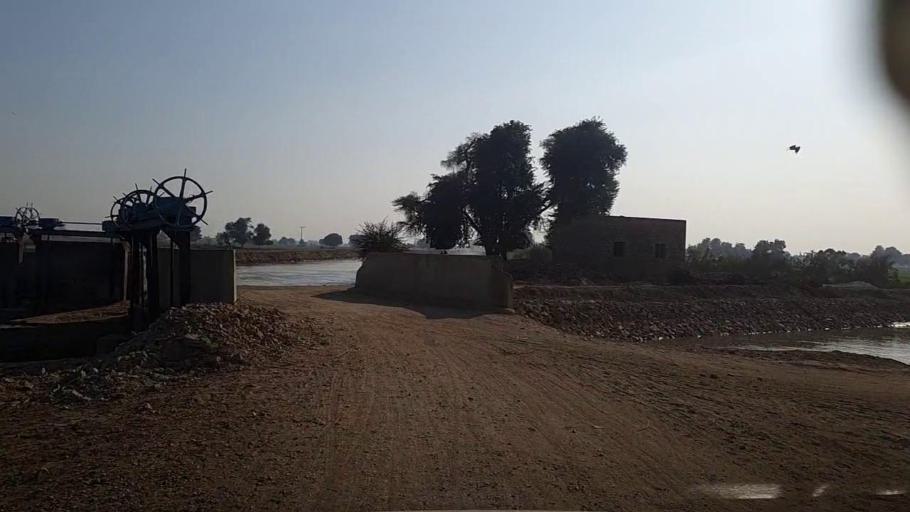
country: PK
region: Sindh
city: Mirpur Mathelo
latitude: 27.8702
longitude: 69.6333
